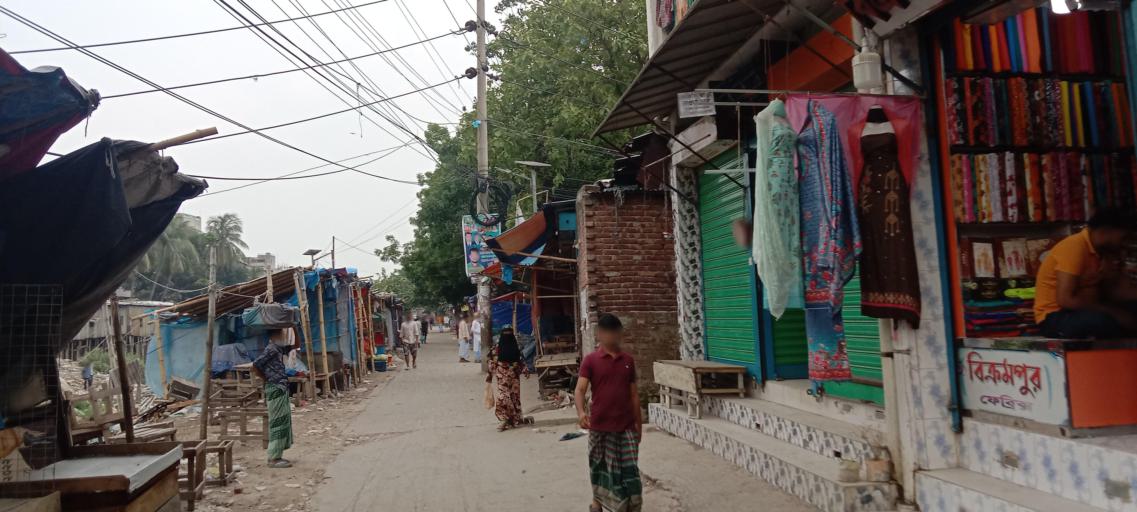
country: BD
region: Dhaka
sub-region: Dhaka
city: Dhaka
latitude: 23.6997
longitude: 90.4078
